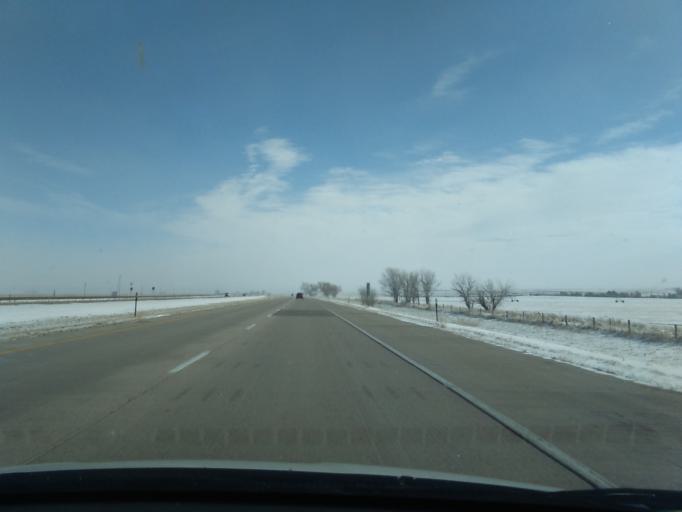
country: US
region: Wyoming
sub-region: Laramie County
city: Pine Bluffs
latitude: 41.1491
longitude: -104.1871
